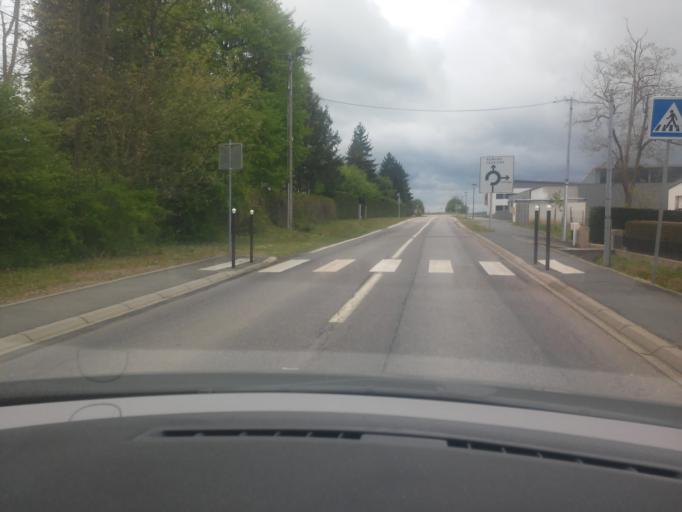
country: FR
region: Lorraine
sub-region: Departement de la Moselle
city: Verny
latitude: 49.0032
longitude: 6.2009
